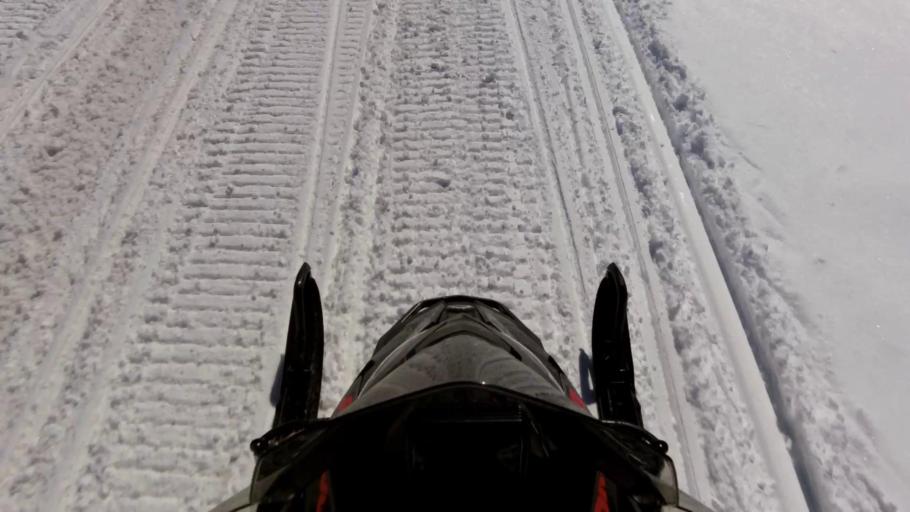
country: US
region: New York
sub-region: Cattaraugus County
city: Franklinville
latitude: 42.3957
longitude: -78.4730
